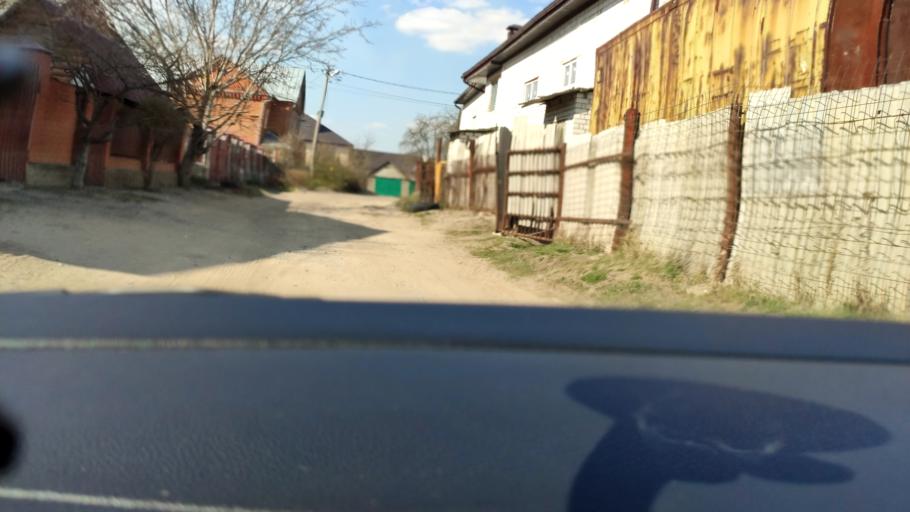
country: RU
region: Voronezj
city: Pridonskoy
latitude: 51.6574
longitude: 39.0872
